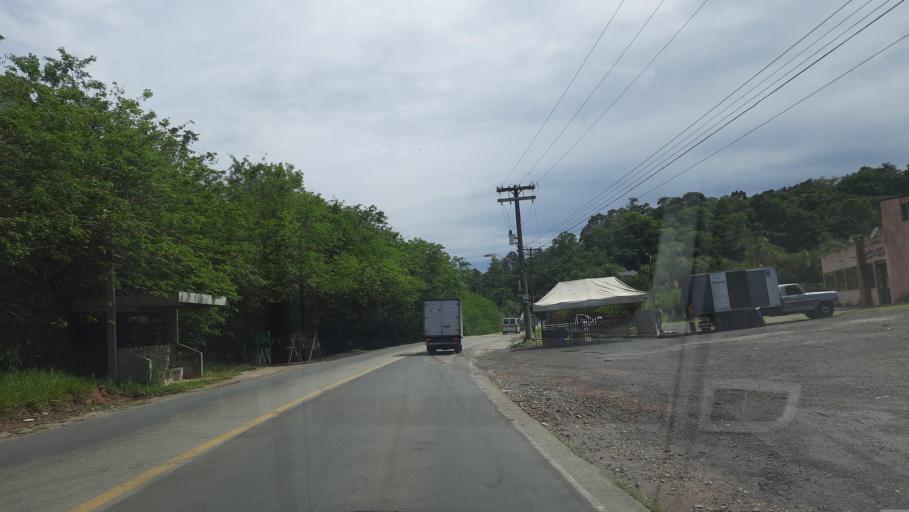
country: BR
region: Sao Paulo
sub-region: Franco Da Rocha
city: Franco da Rocha
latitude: -23.3550
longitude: -46.6662
